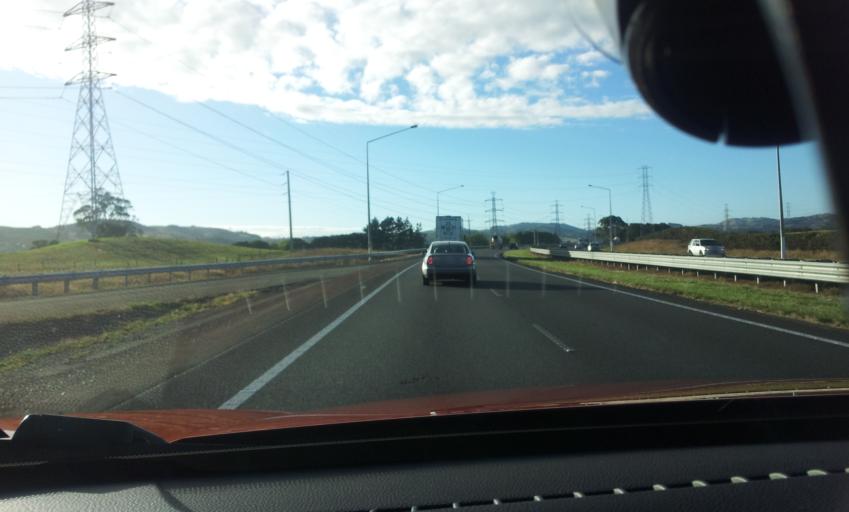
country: NZ
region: Auckland
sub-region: Auckland
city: Papakura
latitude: -37.1183
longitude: 174.9528
